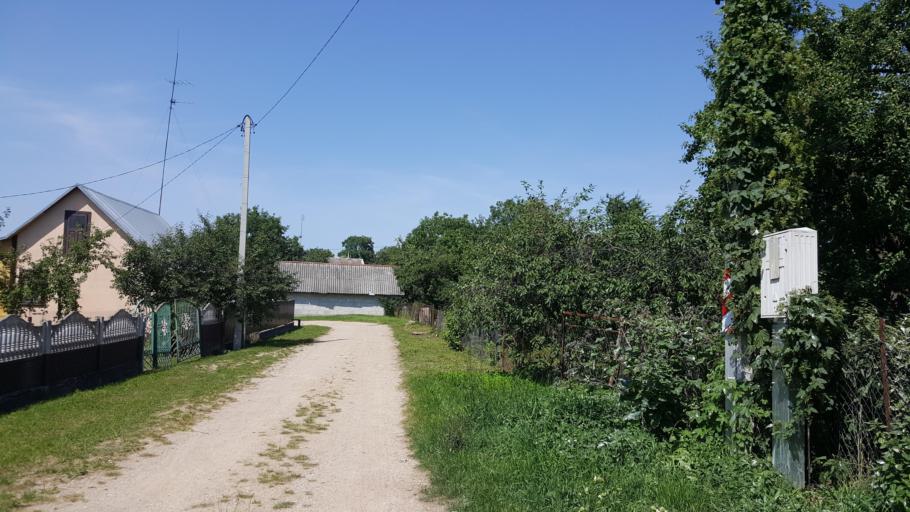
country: BY
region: Brest
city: Vysokaye
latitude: 52.3634
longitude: 23.3809
